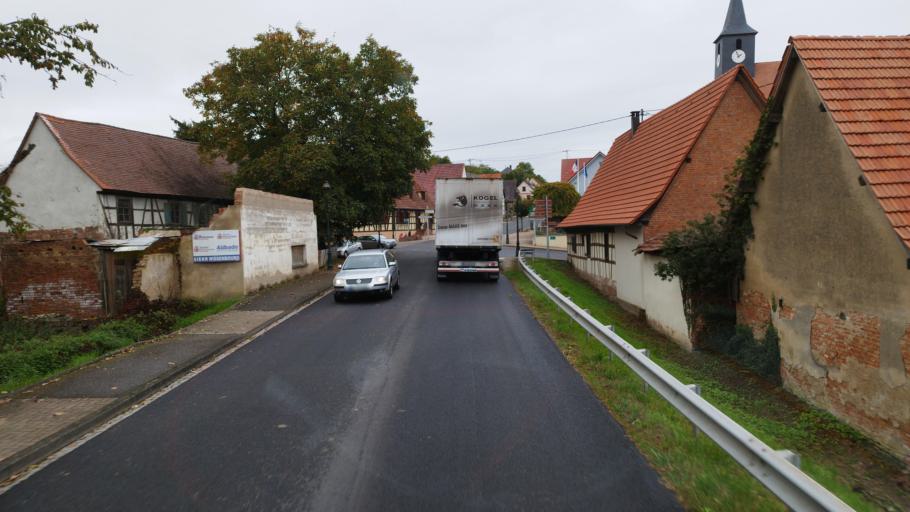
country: FR
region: Alsace
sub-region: Departement du Bas-Rhin
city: Seltz
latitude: 48.9342
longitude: 8.1039
